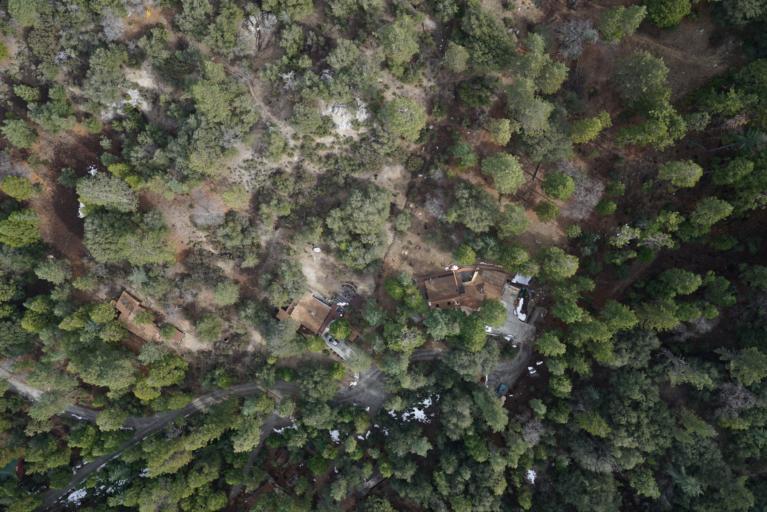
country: US
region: California
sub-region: Riverside County
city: Idyllwild
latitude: 33.7308
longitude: -116.7080
